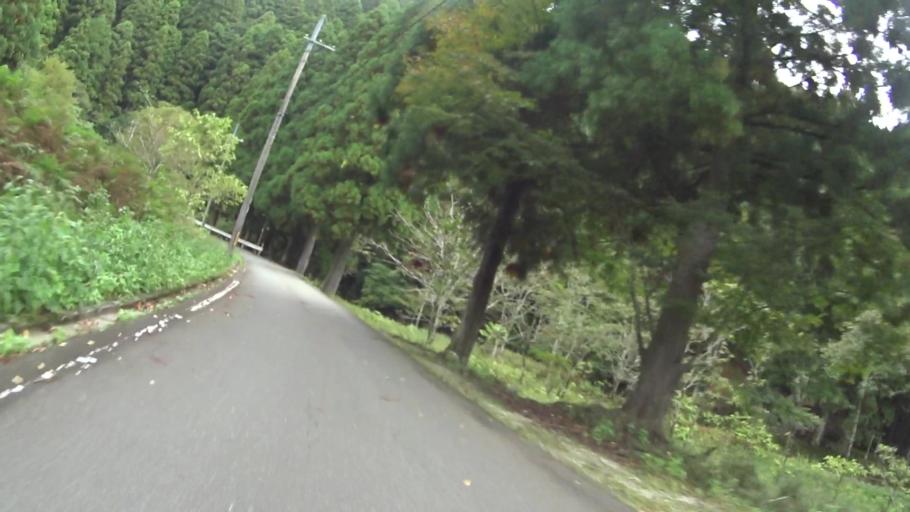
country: JP
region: Fukui
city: Obama
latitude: 35.2950
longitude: 135.6962
